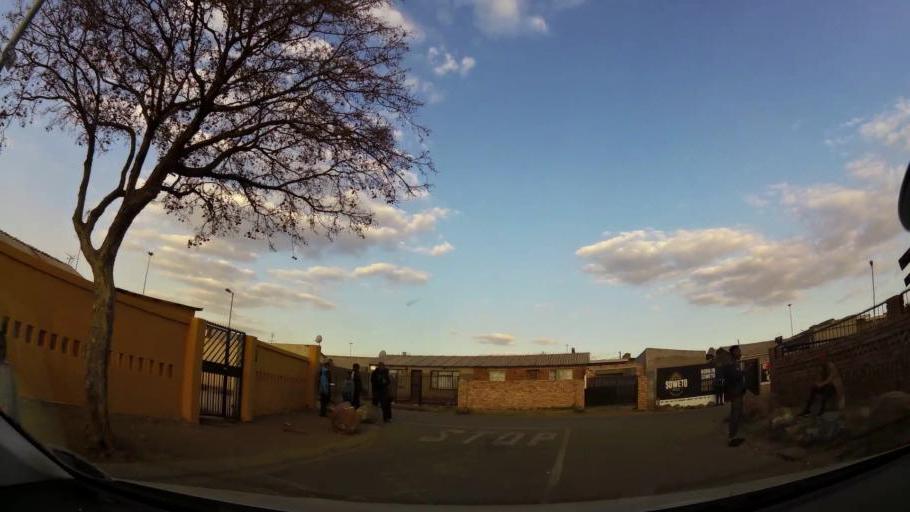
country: ZA
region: Gauteng
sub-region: City of Johannesburg Metropolitan Municipality
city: Soweto
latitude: -26.2707
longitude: 27.8940
